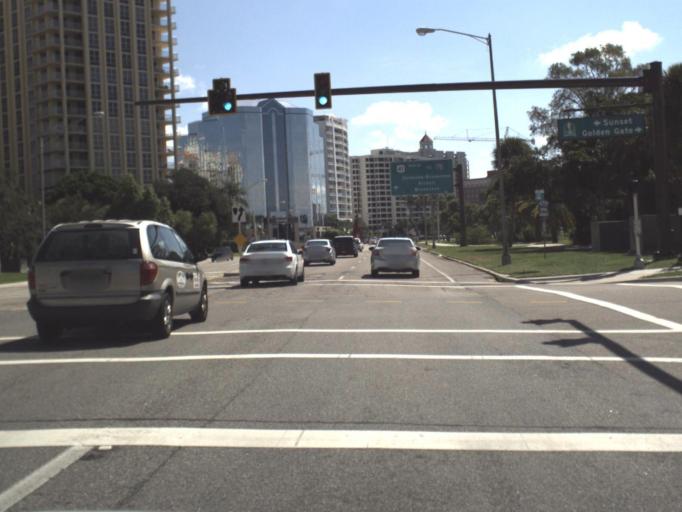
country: US
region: Florida
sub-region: Sarasota County
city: Sarasota
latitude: 27.3357
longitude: -82.5502
